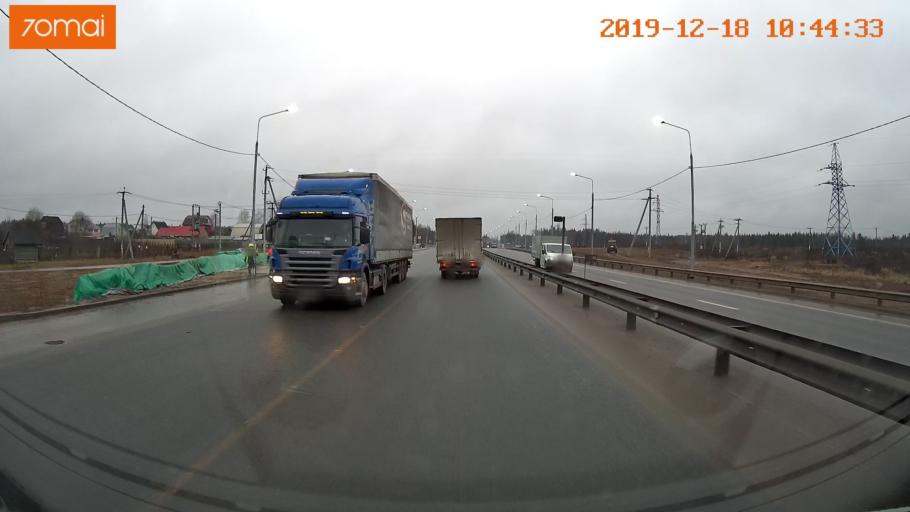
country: RU
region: Moskovskaya
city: Aprelevka
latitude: 55.4735
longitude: 37.0706
